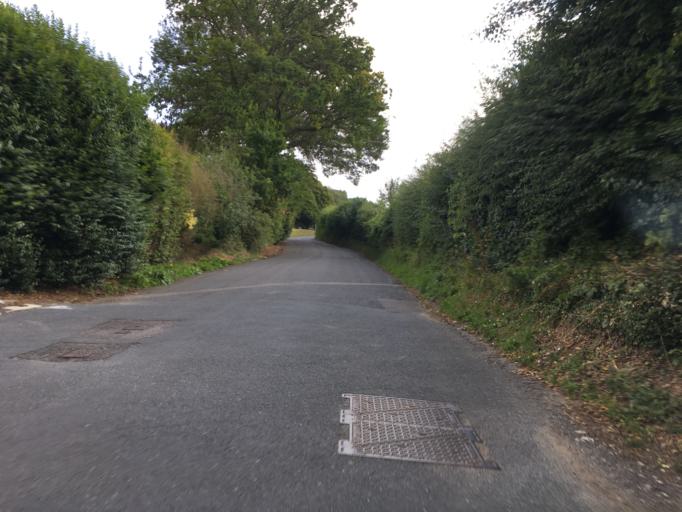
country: GB
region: England
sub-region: Kent
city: Maidstone
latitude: 51.2380
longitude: 0.5162
